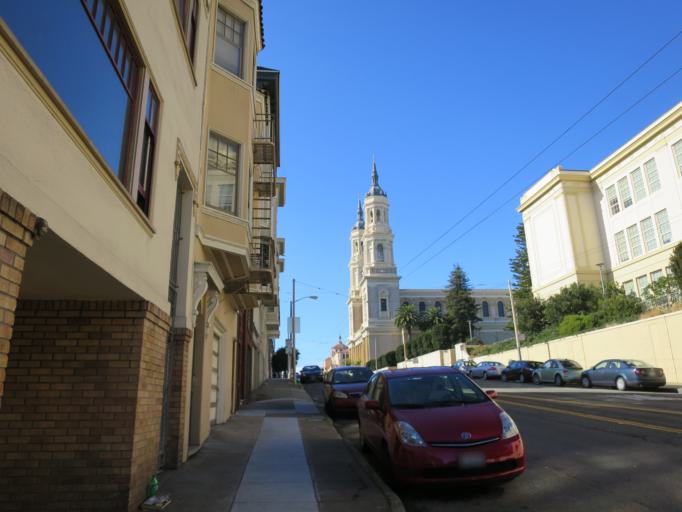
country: US
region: California
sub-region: San Francisco County
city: San Francisco
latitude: 37.7752
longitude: -122.4507
